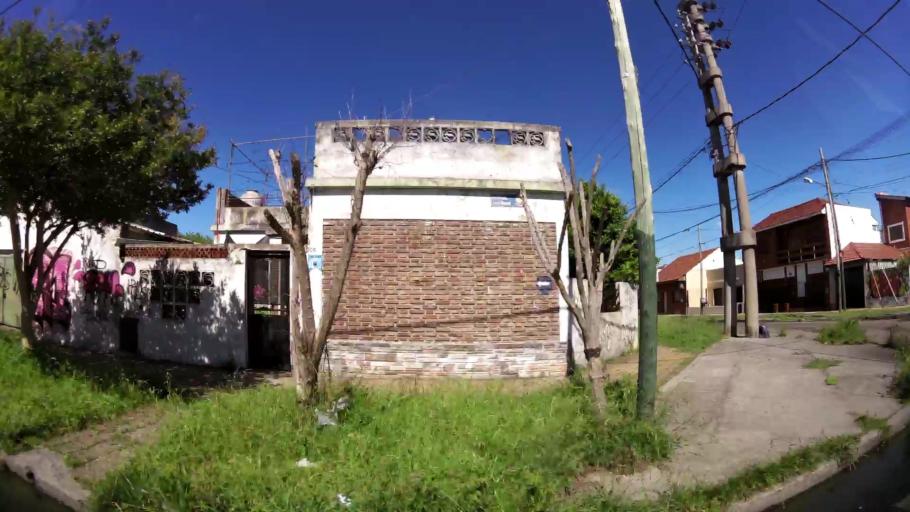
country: AR
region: Buenos Aires
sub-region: Partido de Lomas de Zamora
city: Lomas de Zamora
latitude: -34.7436
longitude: -58.4172
